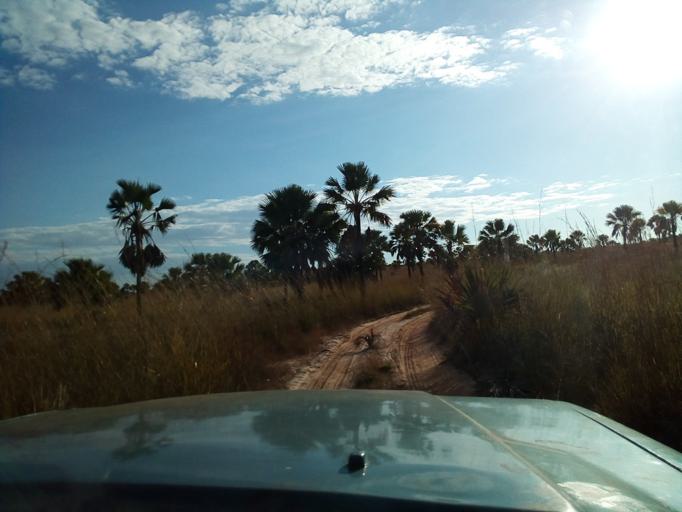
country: MG
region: Boeny
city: Sitampiky
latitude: -16.1505
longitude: 45.5618
